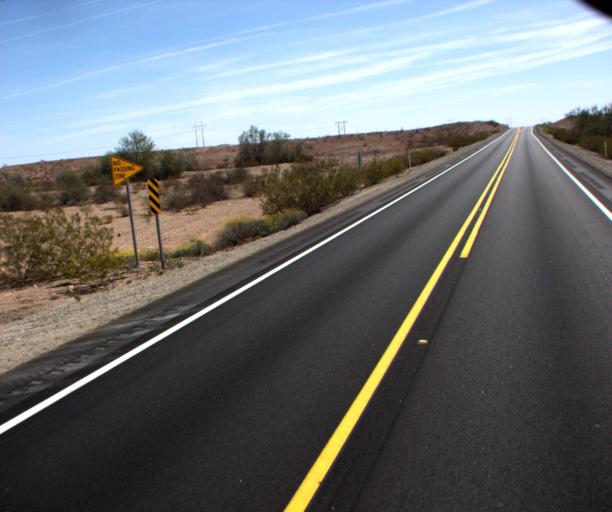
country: US
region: Arizona
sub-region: Yuma County
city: Wellton
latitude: 33.0280
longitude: -114.2879
